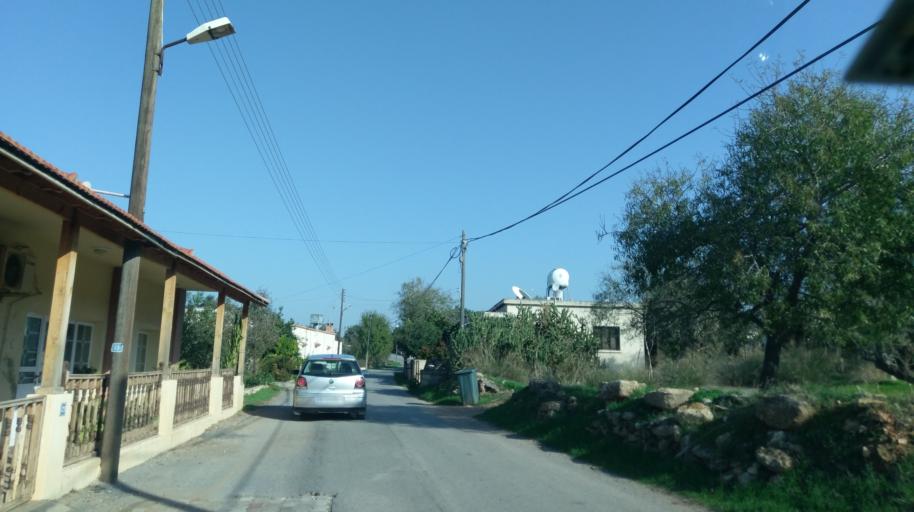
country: CY
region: Ammochostos
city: Leonarisso
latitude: 35.5349
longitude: 34.1942
